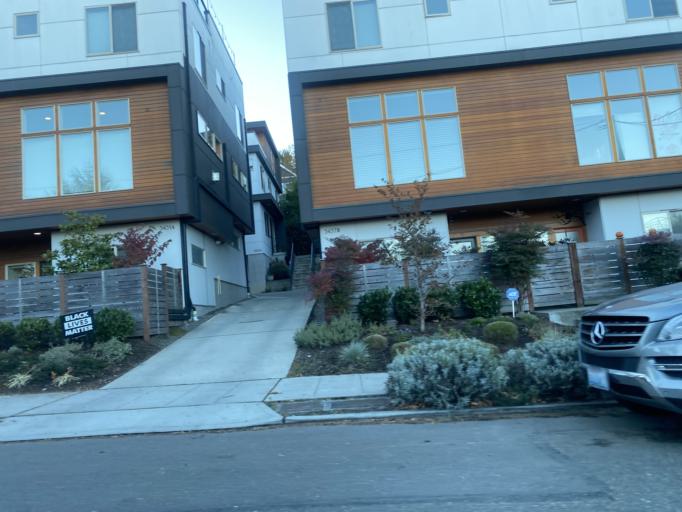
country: US
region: Washington
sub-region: King County
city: Seattle
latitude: 47.6513
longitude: -122.3847
